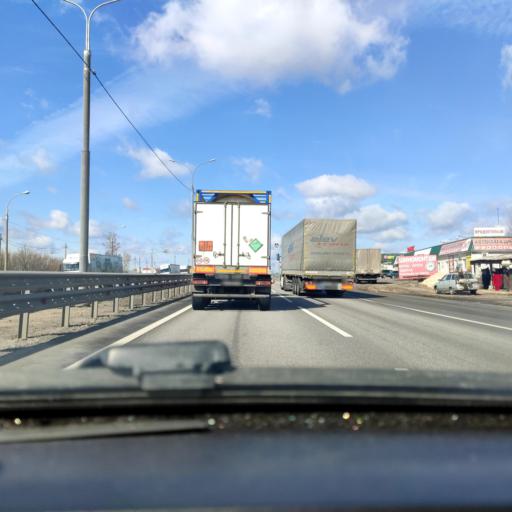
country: RU
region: Lipetsk
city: Khlevnoye
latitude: 52.0786
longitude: 39.1834
